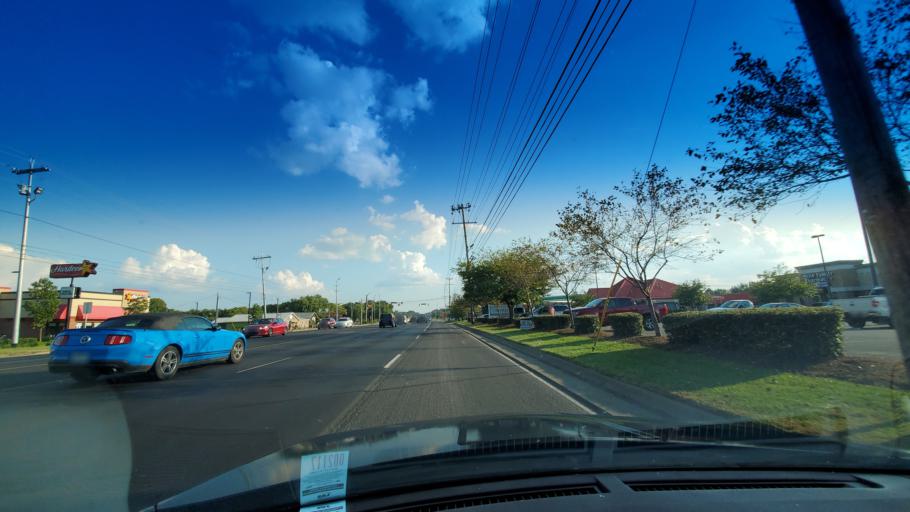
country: US
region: Tennessee
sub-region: Rutherford County
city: Murfreesboro
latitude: 35.7873
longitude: -86.4006
